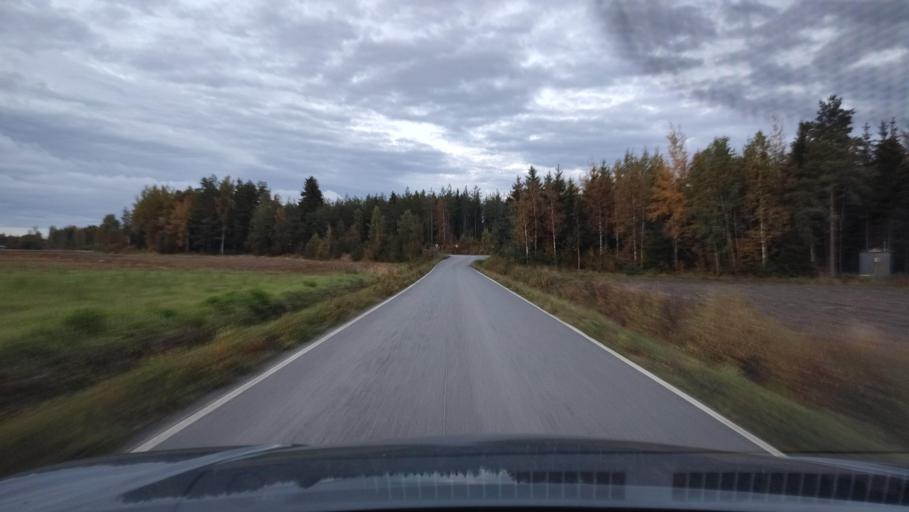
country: FI
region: Ostrobothnia
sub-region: Sydosterbotten
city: Kristinestad
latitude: 62.2753
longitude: 21.5143
